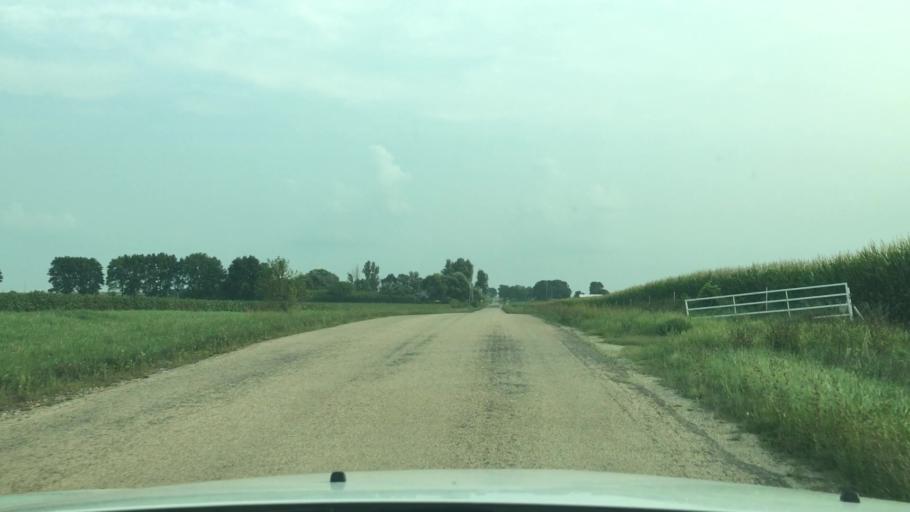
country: US
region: Illinois
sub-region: Ogle County
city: Rochelle
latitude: 41.9234
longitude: -88.9807
